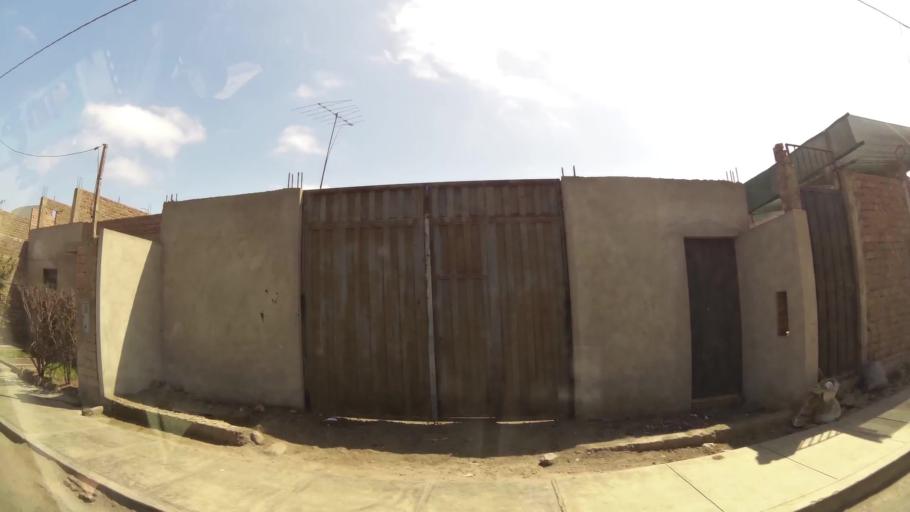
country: PE
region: Lima
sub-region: Provincia de Canete
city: Mala
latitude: -12.6609
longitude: -76.6302
